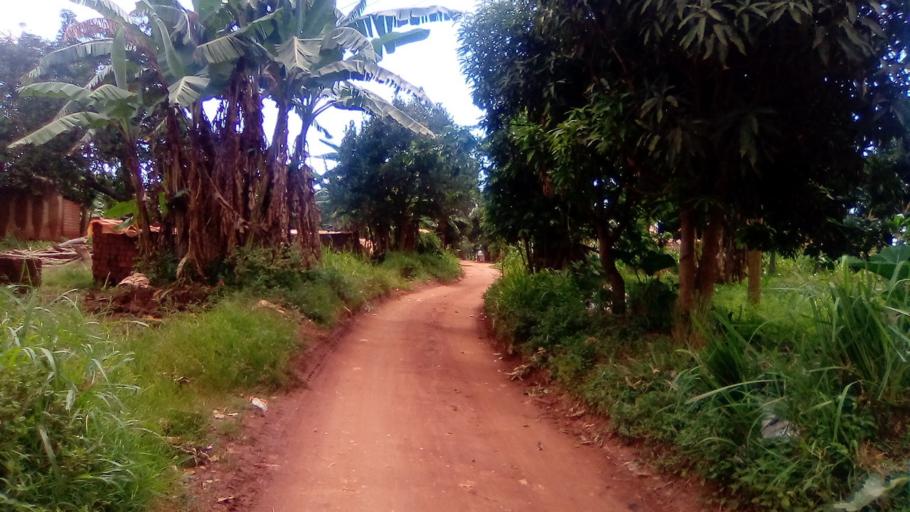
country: UG
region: Central Region
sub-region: Wakiso District
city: Entebbe
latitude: 0.1018
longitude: 32.5276
